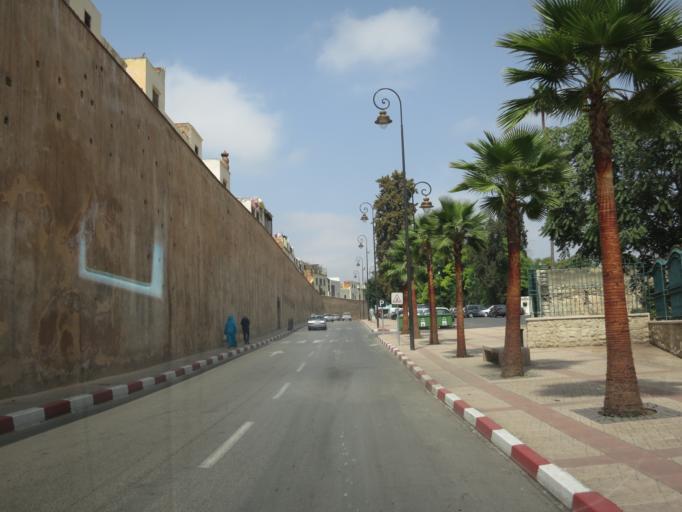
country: MA
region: Meknes-Tafilalet
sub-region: Meknes
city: Meknes
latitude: 33.8948
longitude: -5.5594
